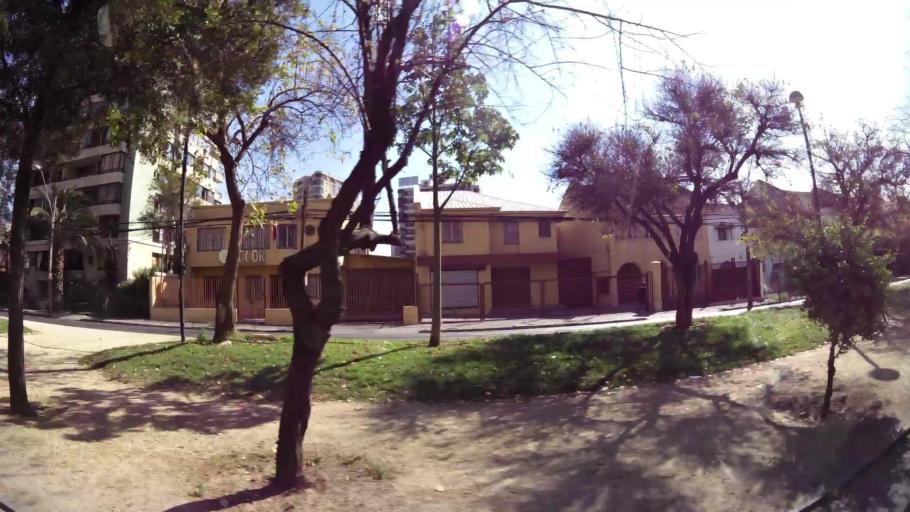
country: CL
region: Santiago Metropolitan
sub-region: Provincia de Santiago
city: Santiago
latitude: -33.4252
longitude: -70.6398
